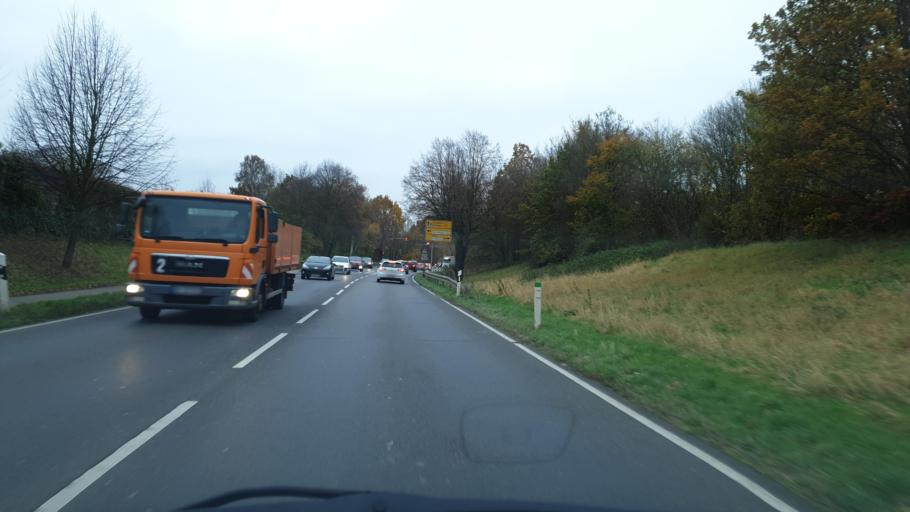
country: DE
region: North Rhine-Westphalia
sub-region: Regierungsbezirk Koln
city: Hurth
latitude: 50.8854
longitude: 6.8624
